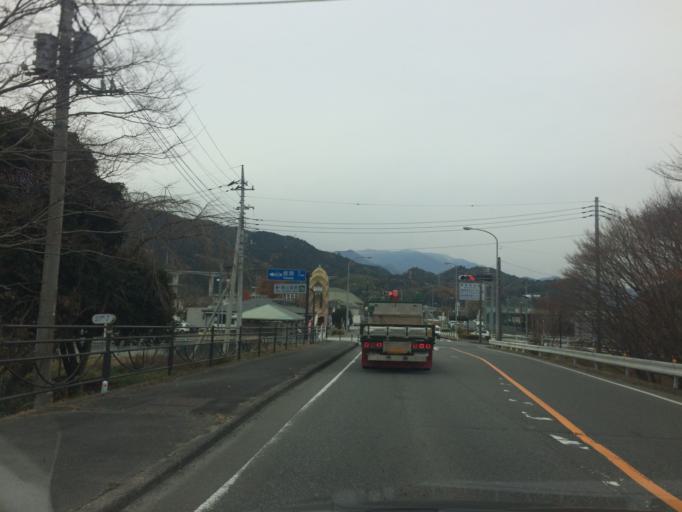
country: JP
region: Shizuoka
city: Fujinomiya
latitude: 35.2411
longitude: 138.4864
